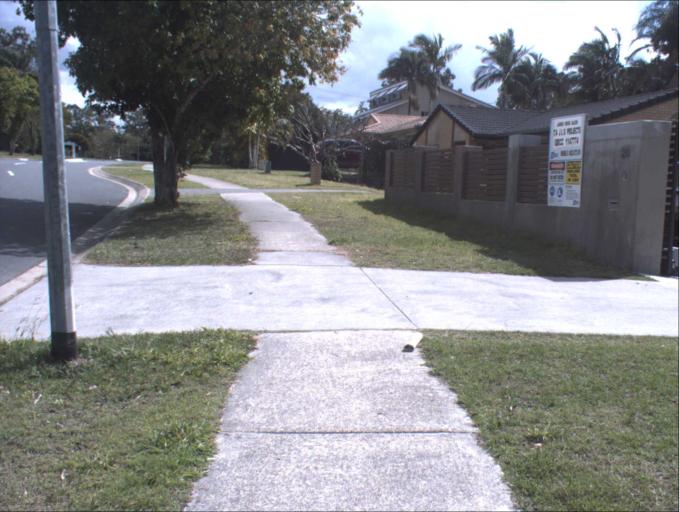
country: AU
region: Queensland
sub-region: Logan
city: Park Ridge South
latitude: -27.6952
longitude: 153.0151
